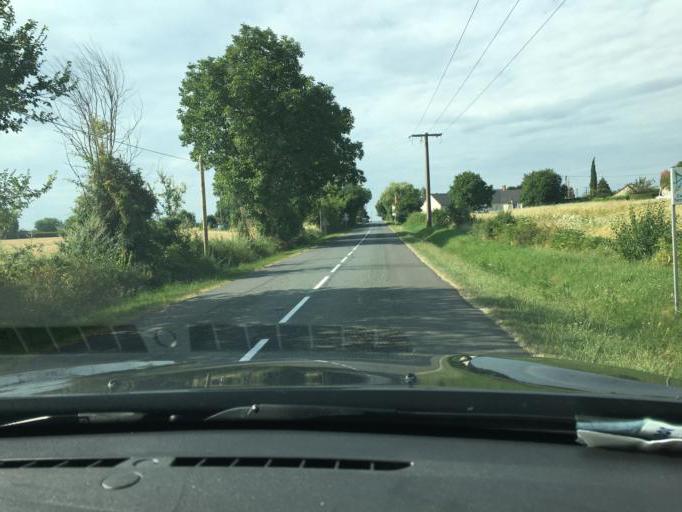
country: FR
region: Centre
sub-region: Departement du Cher
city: Rians
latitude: 47.1753
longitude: 2.6130
